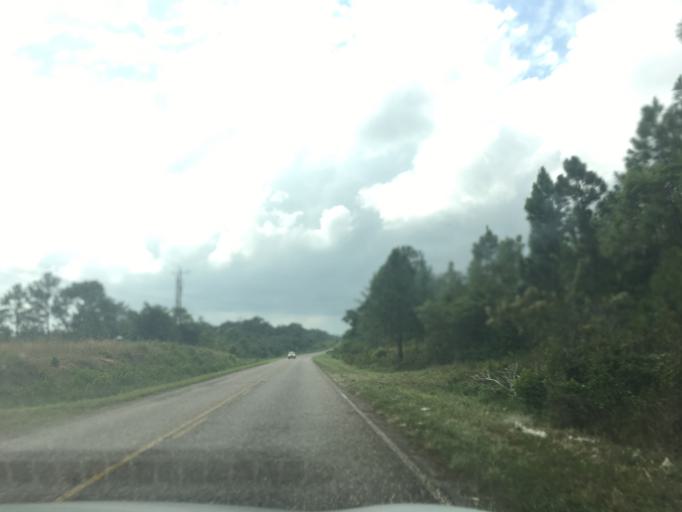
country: BZ
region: Stann Creek
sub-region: Dangriga
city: Dangriga
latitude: 16.9636
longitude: -88.3102
